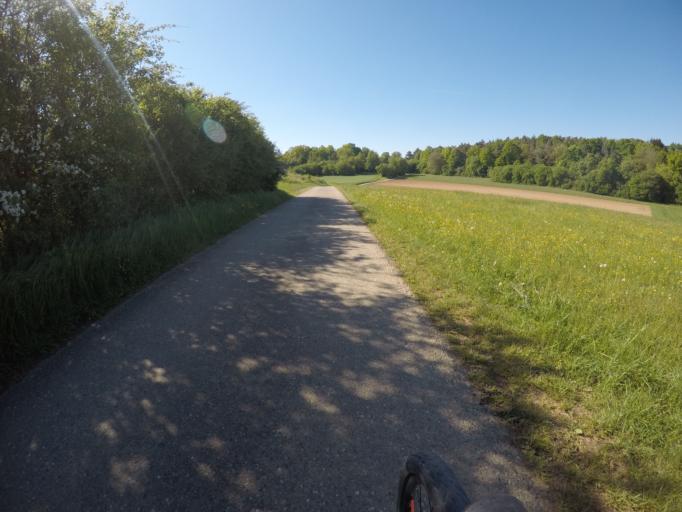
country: DE
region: Baden-Wuerttemberg
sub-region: Karlsruhe Region
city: Friolzheim
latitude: 48.8230
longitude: 8.8507
